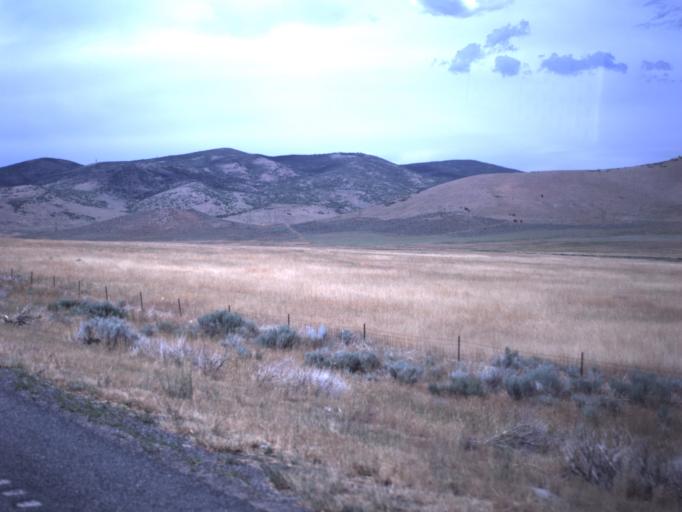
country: US
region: Utah
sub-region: Sanpete County
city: Fountain Green
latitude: 39.6693
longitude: -111.6621
